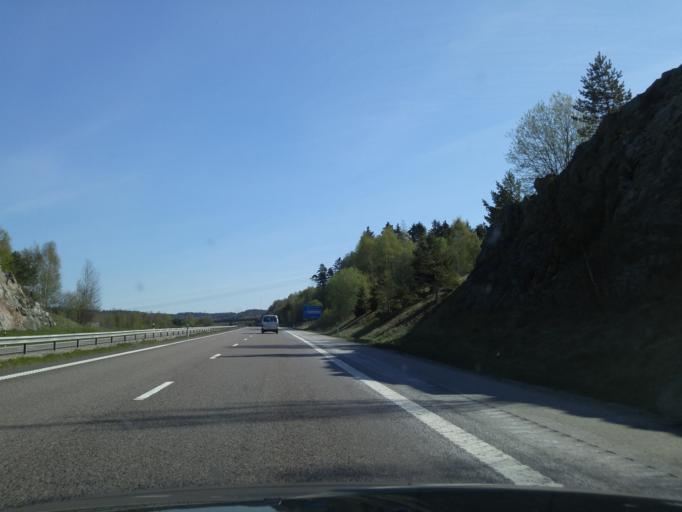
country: SE
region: Vaestra Goetaland
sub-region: Stenungsunds Kommun
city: Stora Hoga
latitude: 58.0524
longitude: 11.8699
